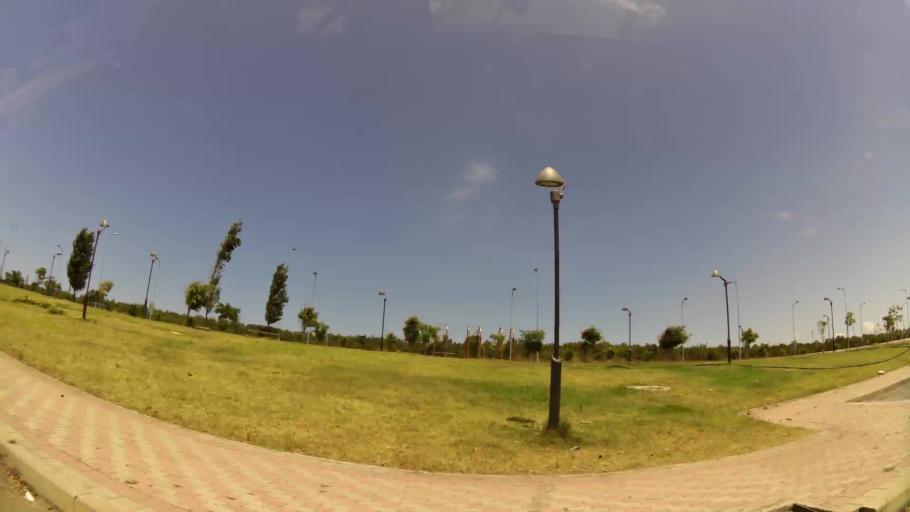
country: MA
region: Gharb-Chrarda-Beni Hssen
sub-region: Kenitra Province
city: Kenitra
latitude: 34.2738
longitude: -6.6156
